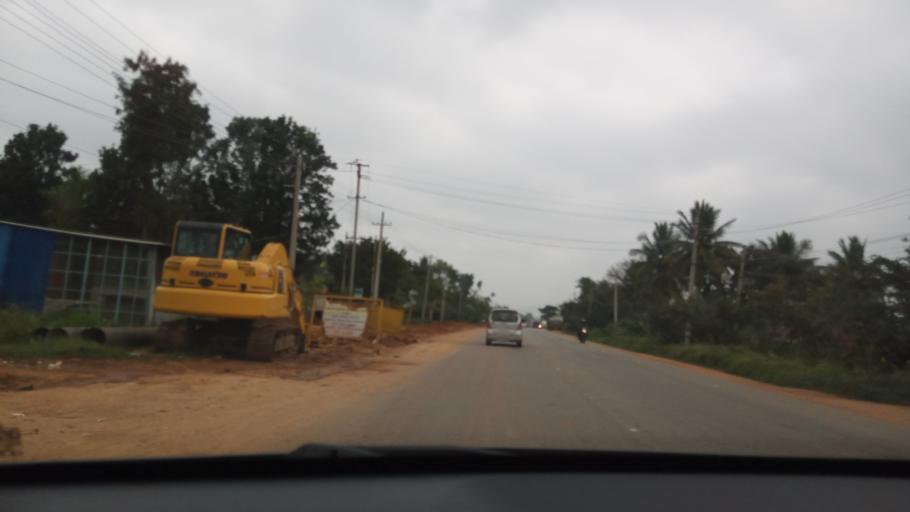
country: IN
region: Karnataka
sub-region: Bangalore Rural
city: Vijayapura
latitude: 13.2617
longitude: 77.9439
